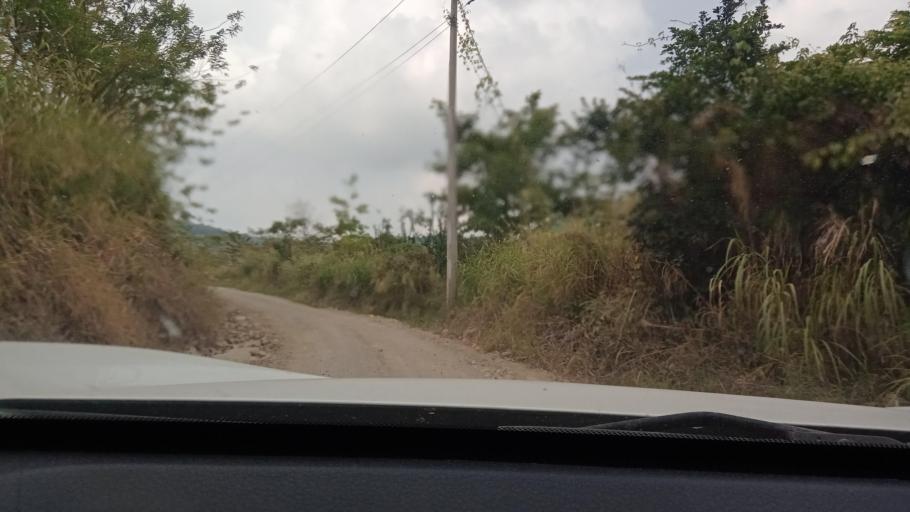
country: MX
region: Tabasco
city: Chontalpa
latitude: 17.4958
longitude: -93.6516
